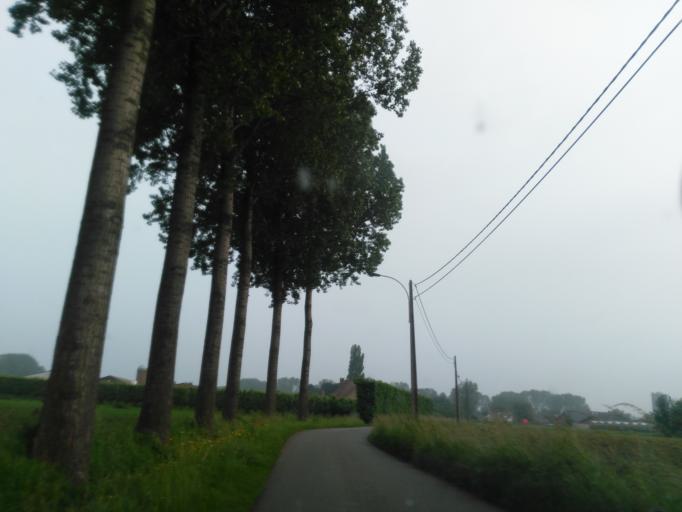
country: BE
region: Flanders
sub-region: Provincie Oost-Vlaanderen
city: Beveren
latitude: 51.2020
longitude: 4.2745
